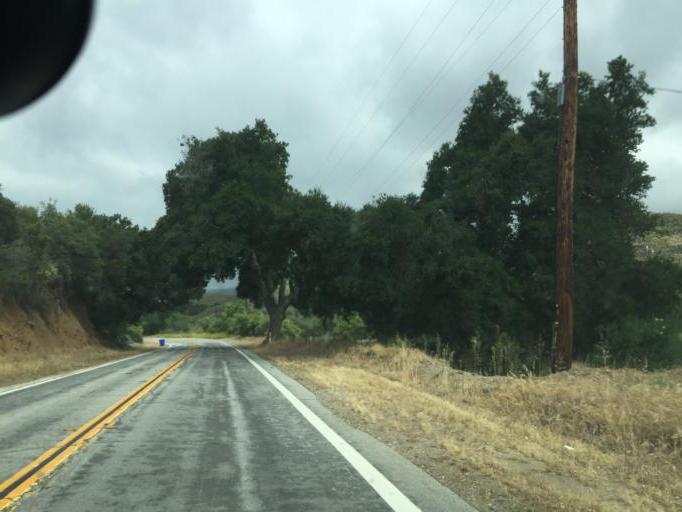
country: US
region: California
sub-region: Los Angeles County
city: Leona Valley
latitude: 34.5830
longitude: -118.3390
